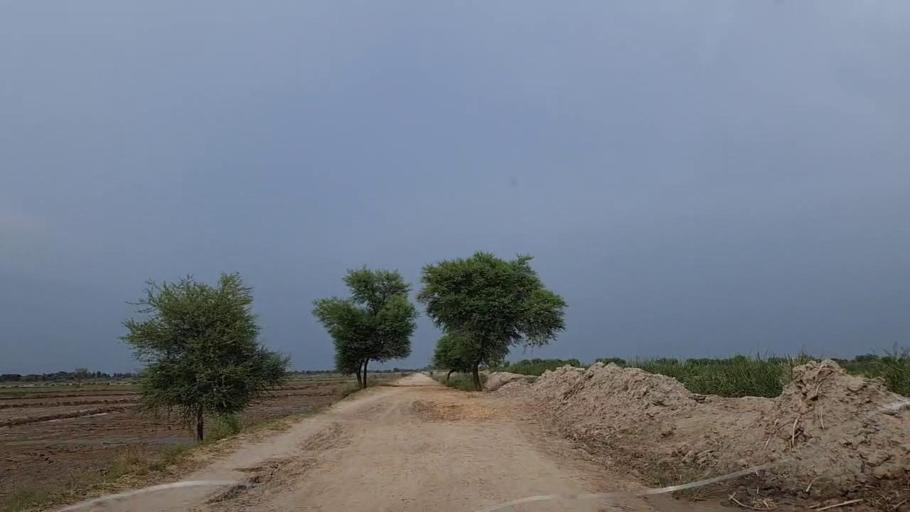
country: PK
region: Sindh
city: Khanpur
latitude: 27.8361
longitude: 69.5818
